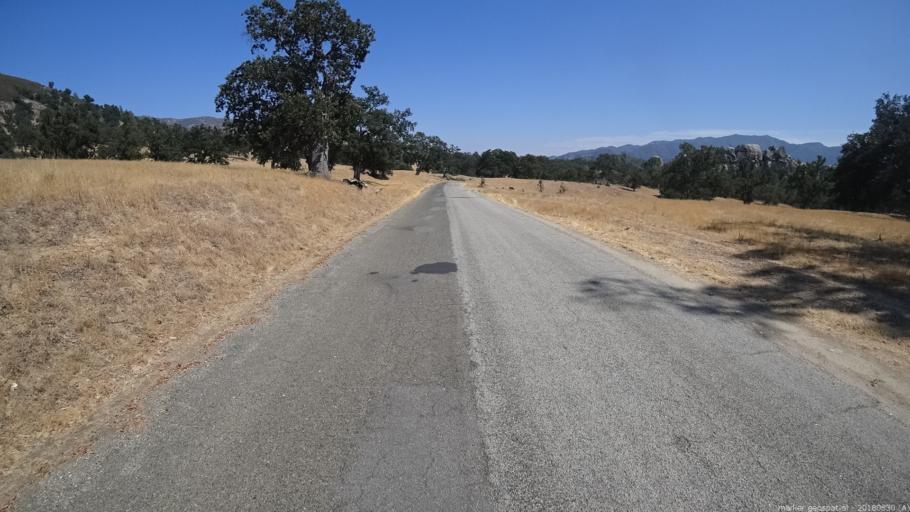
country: US
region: California
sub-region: Monterey County
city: Greenfield
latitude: 36.0880
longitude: -121.4074
